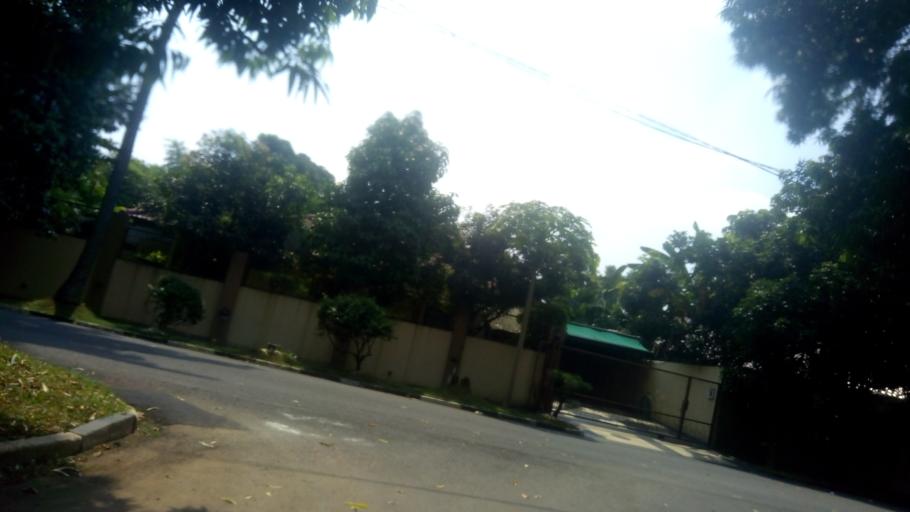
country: ID
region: Jakarta Raya
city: Jakarta
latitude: -6.2378
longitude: 106.8340
